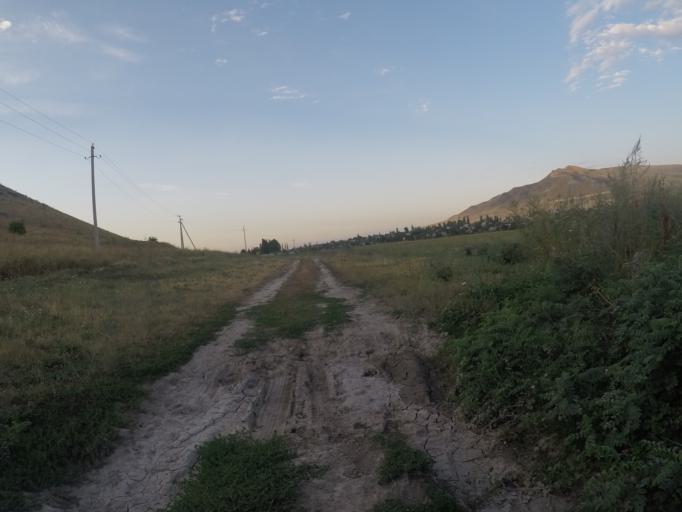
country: KG
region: Chuy
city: Bishkek
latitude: 42.7616
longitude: 74.6368
